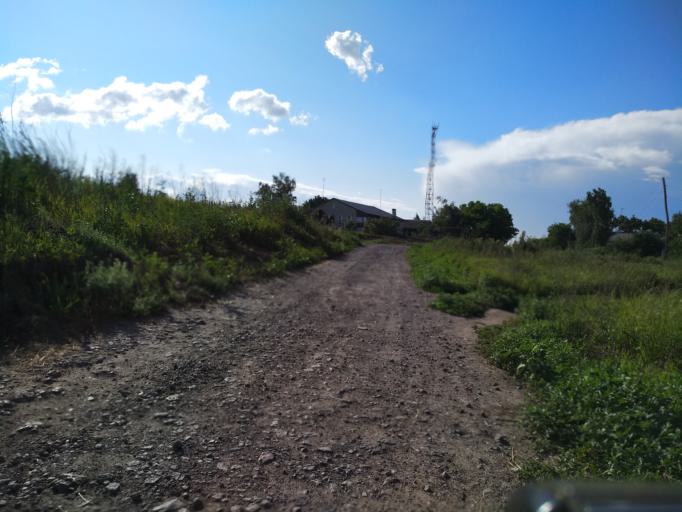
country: RU
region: Lipetsk
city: Dobrinka
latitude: 52.0343
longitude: 40.5603
